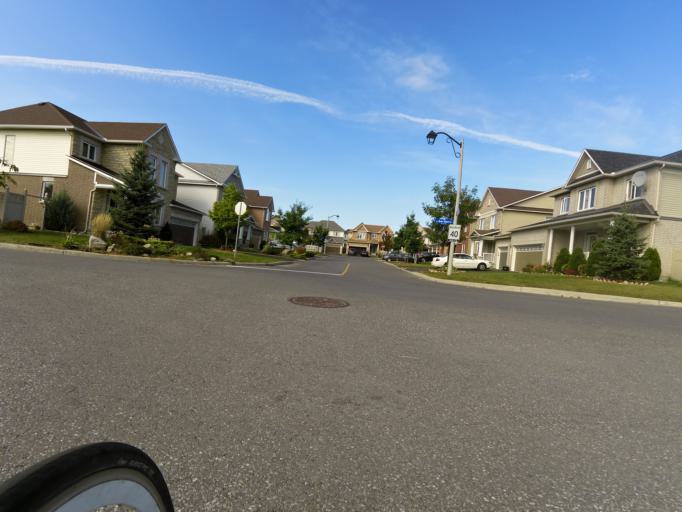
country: CA
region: Ontario
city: Bells Corners
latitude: 45.2659
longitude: -75.7281
